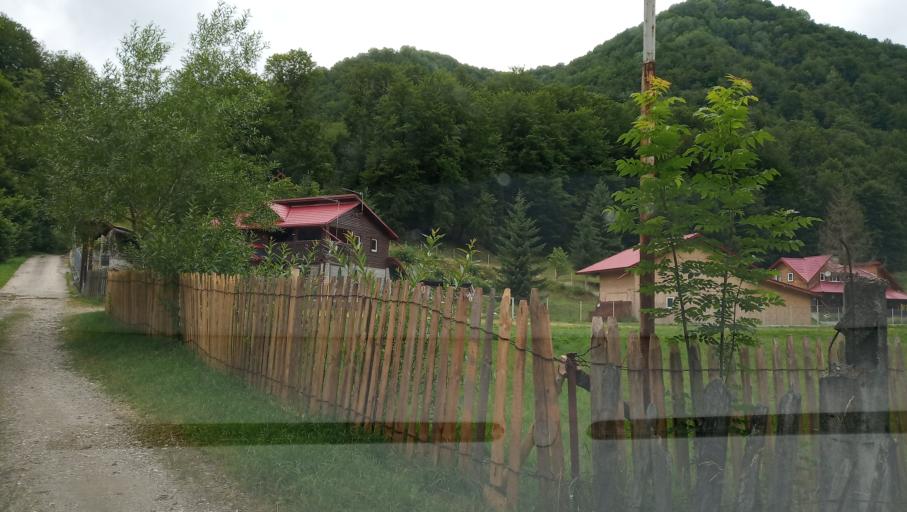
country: RO
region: Hunedoara
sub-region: Oras Petrila
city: Petrila
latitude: 45.4887
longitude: 23.4187
